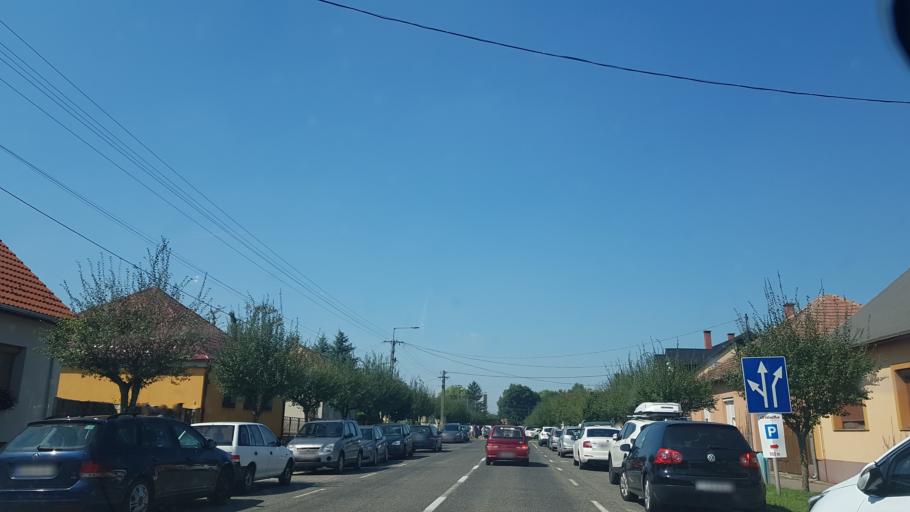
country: HU
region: Somogy
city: Nagyatad
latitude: 46.2347
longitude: 17.3607
